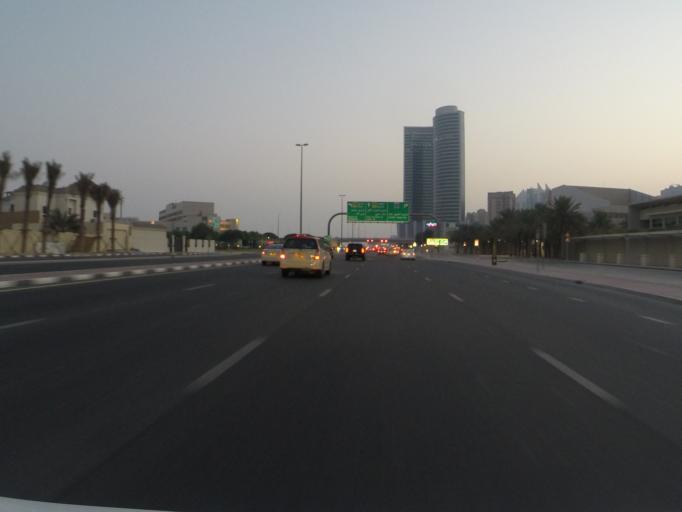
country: AE
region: Dubai
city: Dubai
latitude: 25.1002
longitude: 55.1844
